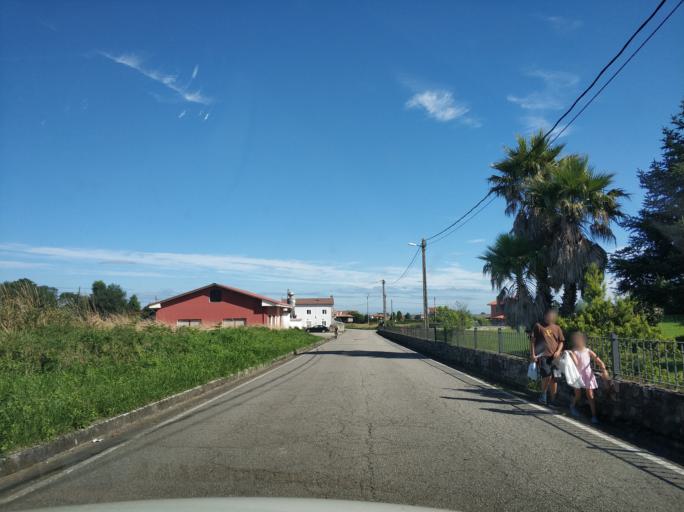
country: ES
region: Asturias
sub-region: Province of Asturias
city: Cudillero
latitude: 43.5709
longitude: -6.2366
